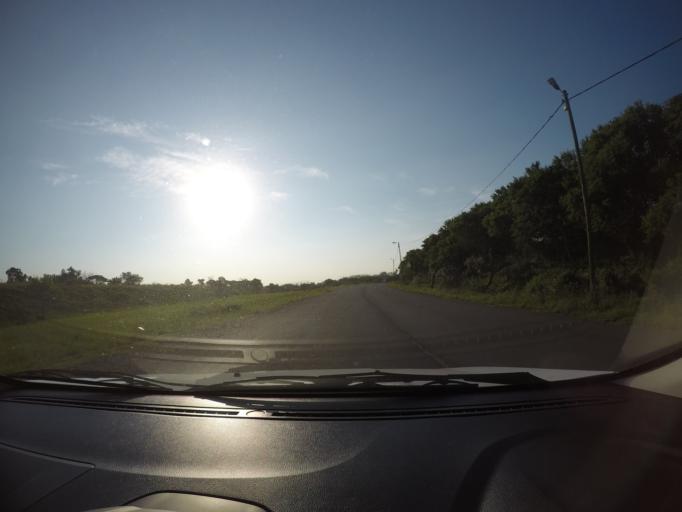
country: ZA
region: KwaZulu-Natal
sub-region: uThungulu District Municipality
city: Richards Bay
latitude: -28.7674
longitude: 32.0048
